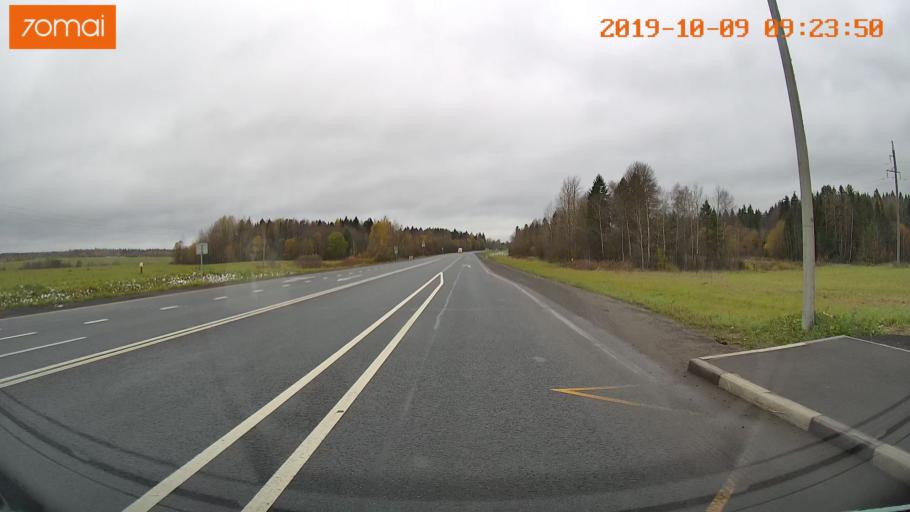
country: RU
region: Vologda
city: Vologda
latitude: 59.0735
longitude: 40.0253
